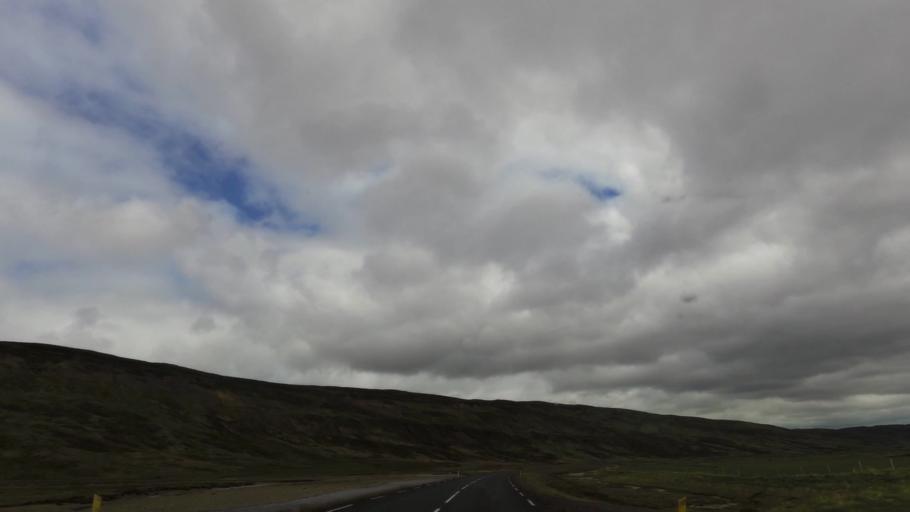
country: IS
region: West
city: Stykkisholmur
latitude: 65.7634
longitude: -21.8387
